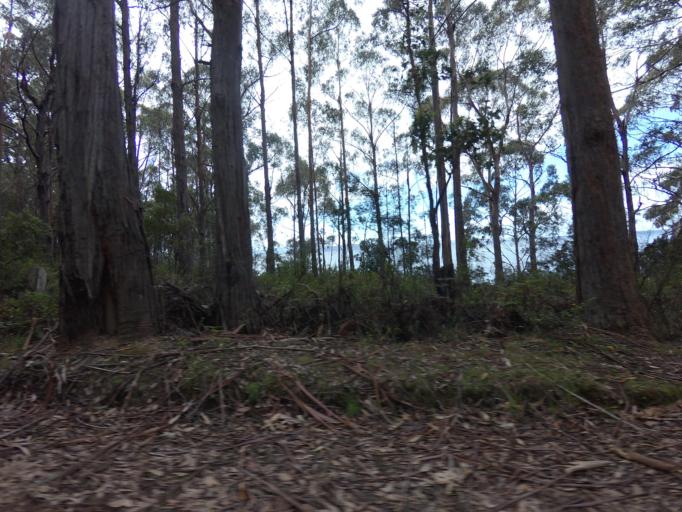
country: AU
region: Tasmania
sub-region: Huon Valley
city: Geeveston
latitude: -43.4175
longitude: 147.0146
